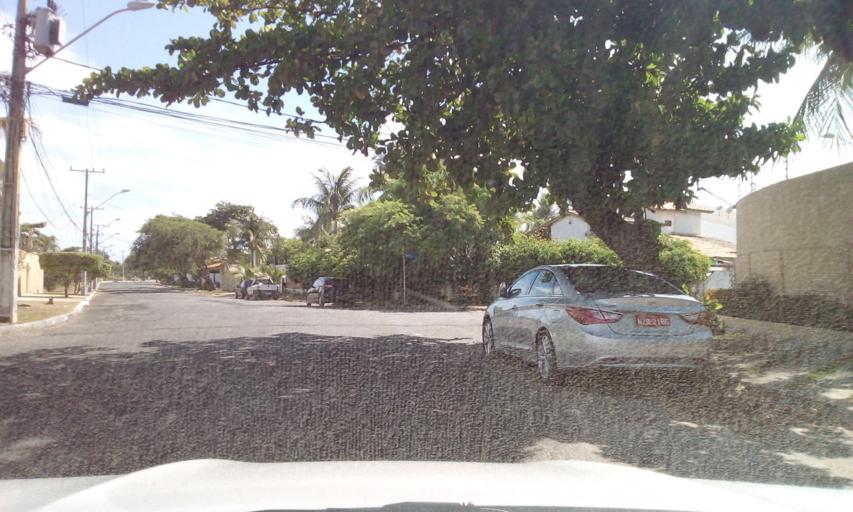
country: BR
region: Bahia
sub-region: Lauro De Freitas
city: Lauro de Freitas
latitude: -12.8880
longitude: -38.2890
